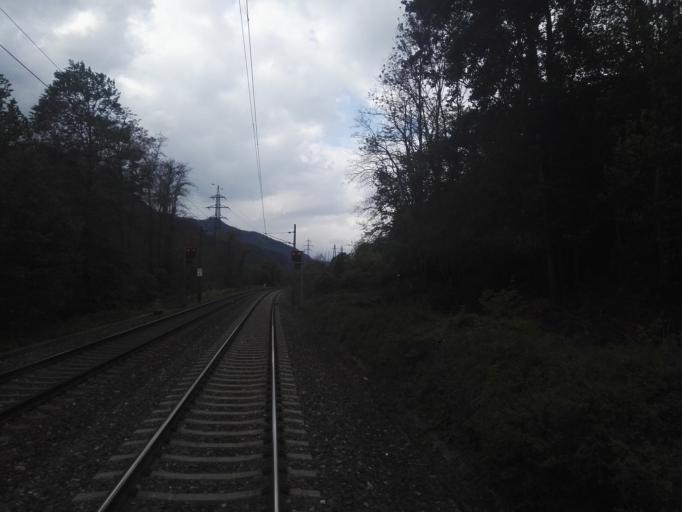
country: AT
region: Styria
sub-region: Politischer Bezirk Graz-Umgebung
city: Rothelstein
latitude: 47.3170
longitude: 15.3729
